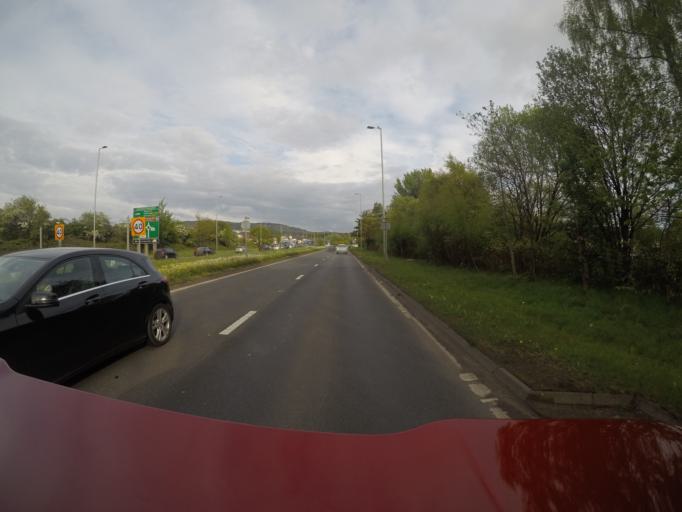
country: GB
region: Scotland
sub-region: West Dunbartonshire
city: Dumbarton
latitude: 55.9572
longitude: -4.5653
